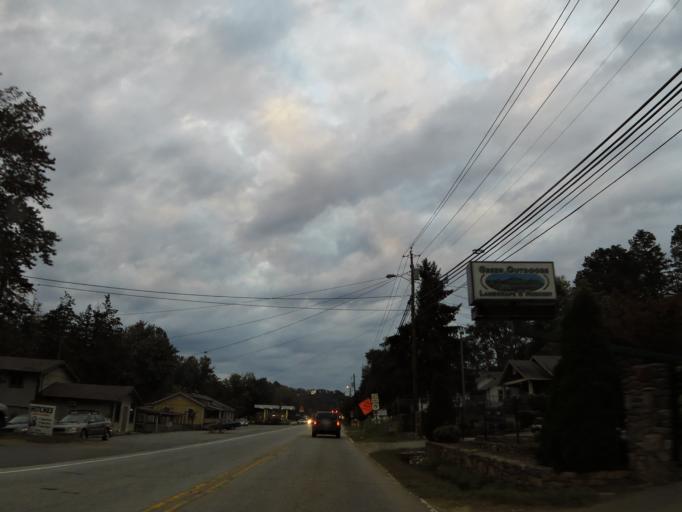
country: US
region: North Carolina
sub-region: Buncombe County
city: Woodfin
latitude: 35.6418
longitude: -82.5792
